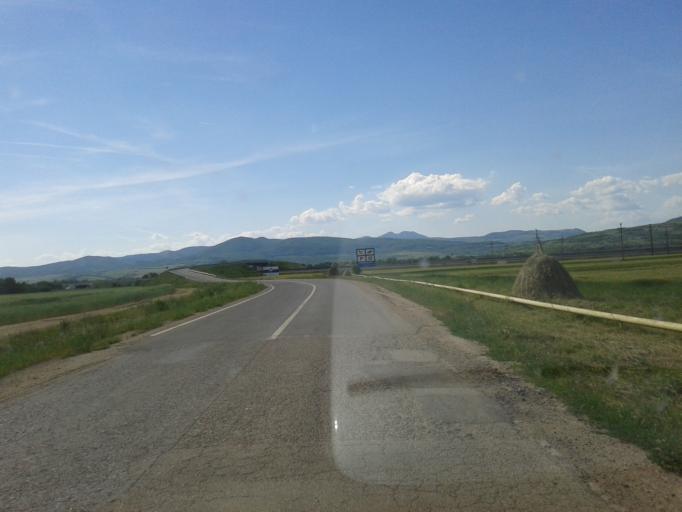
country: RO
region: Hunedoara
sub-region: Comuna Geoagiu
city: Geoagiu
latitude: 45.8850
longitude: 23.2470
